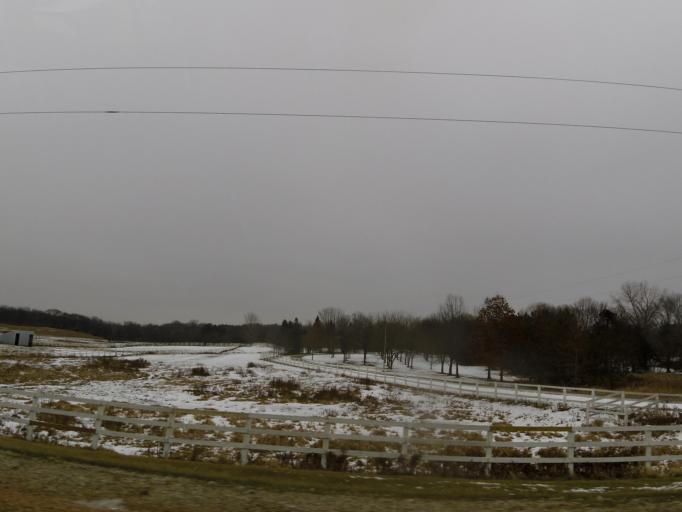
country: US
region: Minnesota
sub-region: Scott County
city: Prior Lake
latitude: 44.6409
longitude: -93.4704
